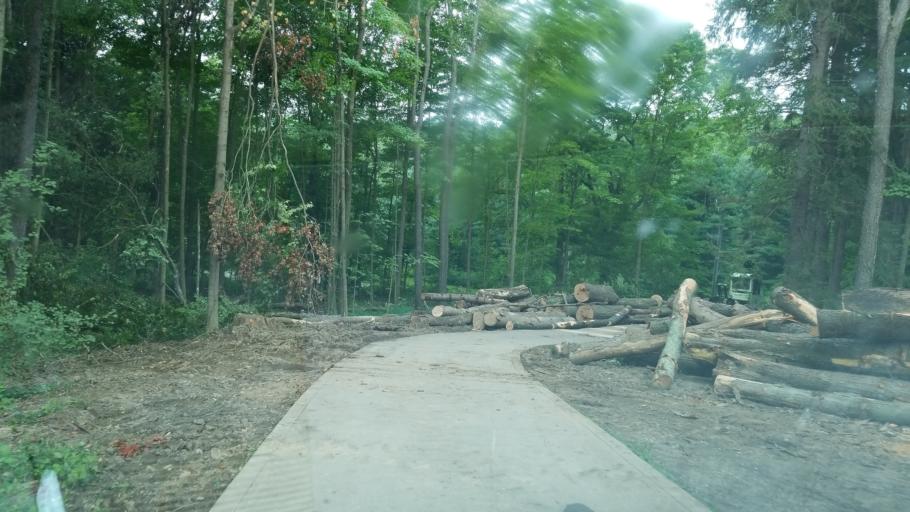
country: US
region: Ohio
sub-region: Sandusky County
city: Bellville
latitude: 40.6170
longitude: -82.5393
